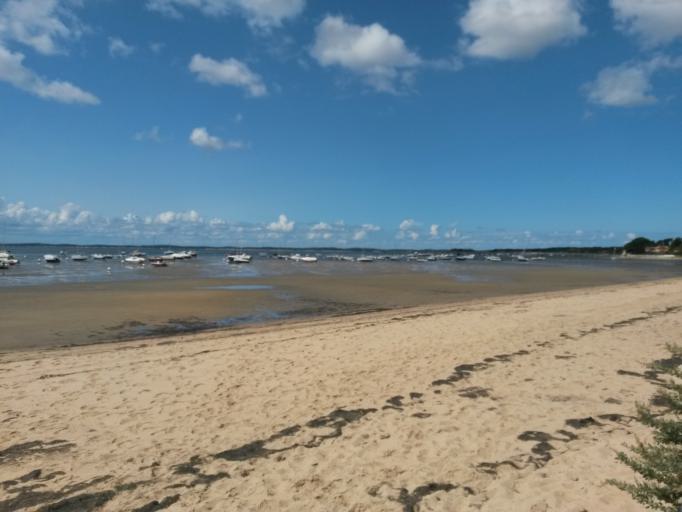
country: FR
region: Aquitaine
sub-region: Departement de la Gironde
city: Andernos-les-Bains
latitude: 44.7342
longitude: -1.0938
